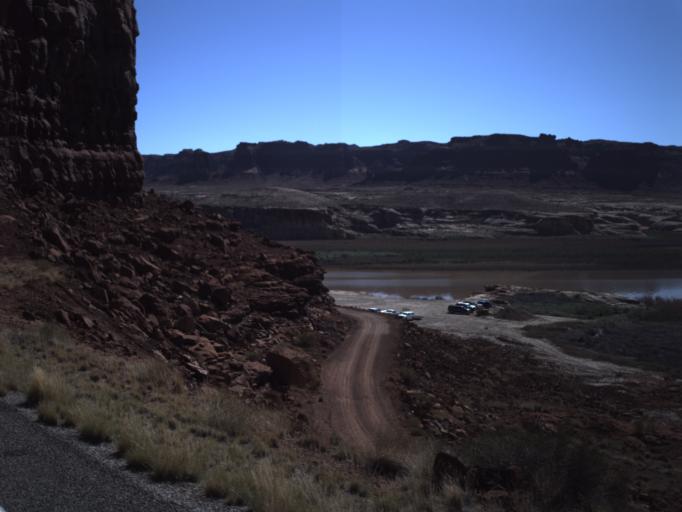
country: US
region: Utah
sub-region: San Juan County
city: Blanding
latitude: 37.8898
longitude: -110.4030
